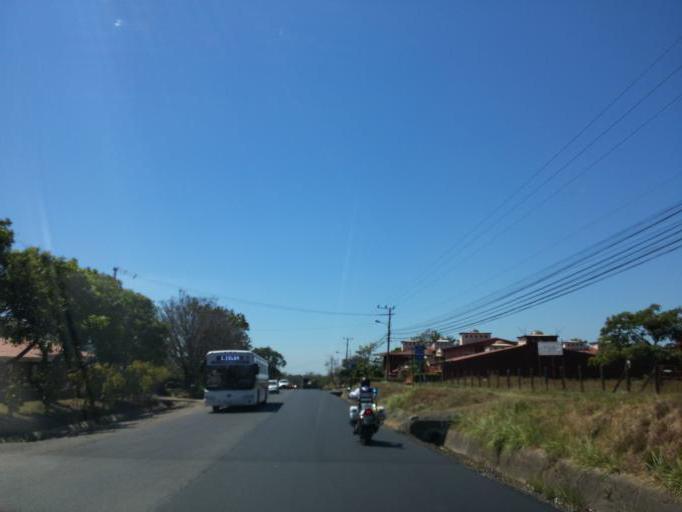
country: CR
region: Heredia
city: Colon
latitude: 9.9345
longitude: -84.2254
